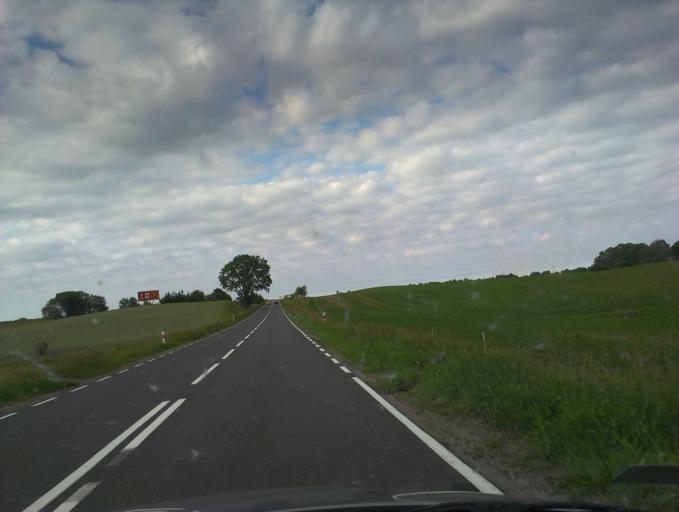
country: PL
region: West Pomeranian Voivodeship
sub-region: Powiat szczecinecki
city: Szczecinek
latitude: 53.6675
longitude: 16.6778
